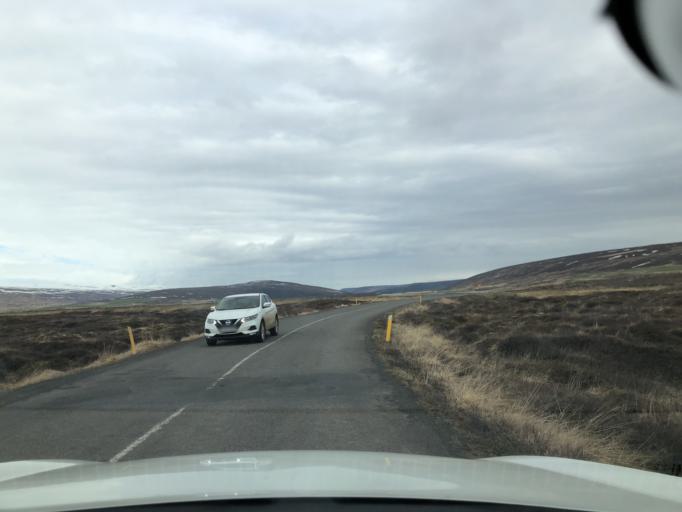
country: IS
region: Northeast
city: Laugar
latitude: 65.6857
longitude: -17.5463
